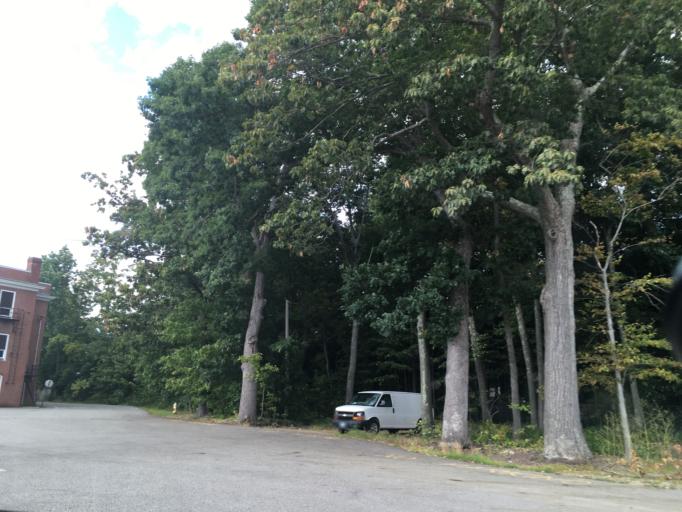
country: US
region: New Hampshire
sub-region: Rockingham County
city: Exeter
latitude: 42.9751
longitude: -70.9552
